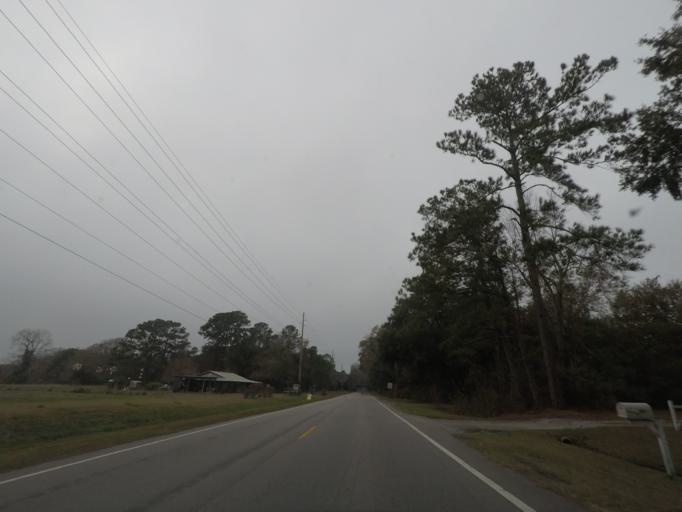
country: US
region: South Carolina
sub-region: Charleston County
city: Seabrook Island
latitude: 32.5812
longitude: -80.3338
